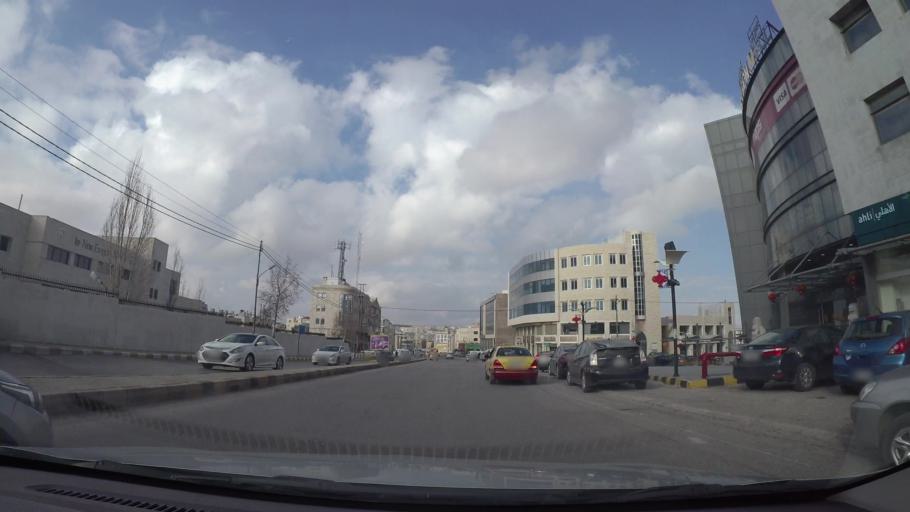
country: JO
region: Amman
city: Al Jubayhah
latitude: 31.9865
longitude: 35.8479
